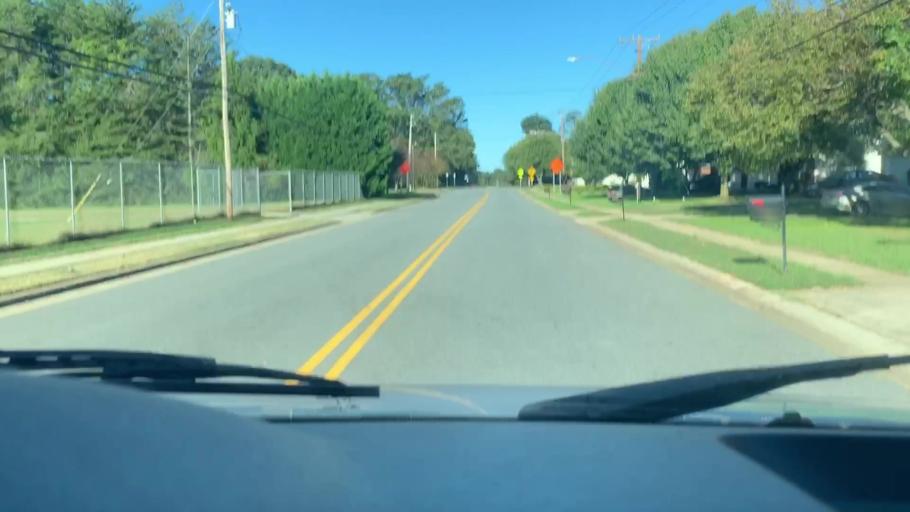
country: US
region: North Carolina
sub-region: Mecklenburg County
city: Charlotte
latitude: 35.2908
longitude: -80.7876
